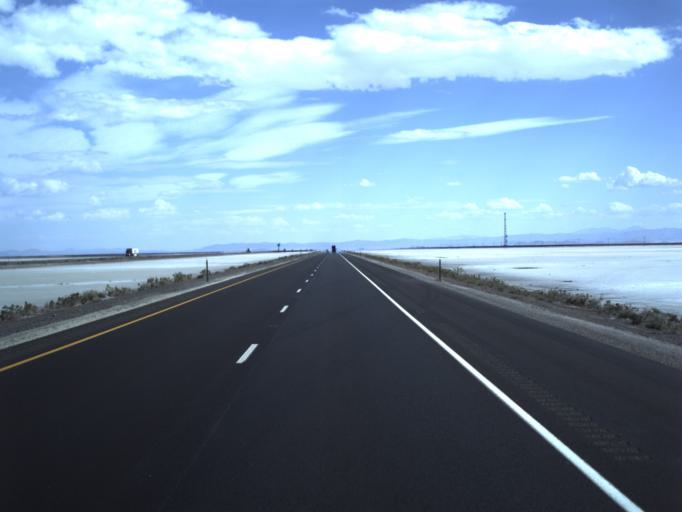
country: US
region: Utah
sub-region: Tooele County
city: Wendover
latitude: 40.7328
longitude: -113.5852
